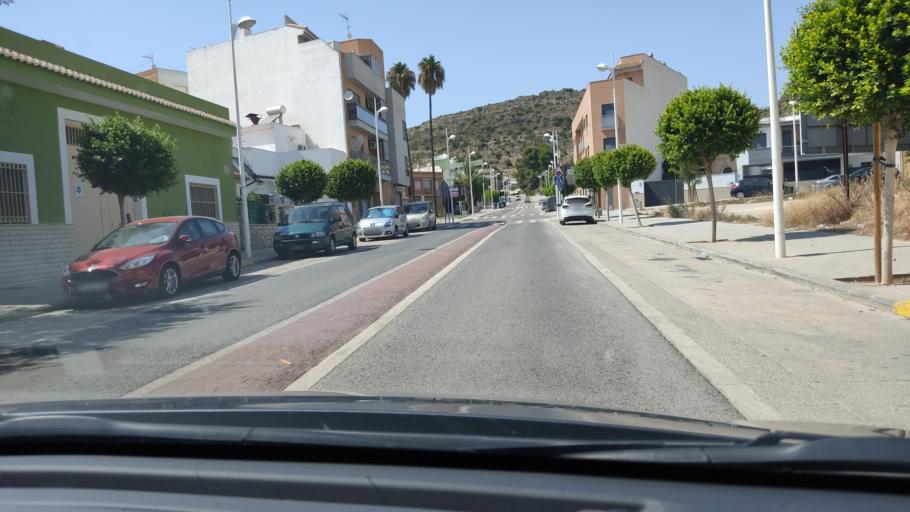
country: ES
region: Valencia
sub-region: Provincia de Valencia
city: Monserrat
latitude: 39.3583
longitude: -0.5980
